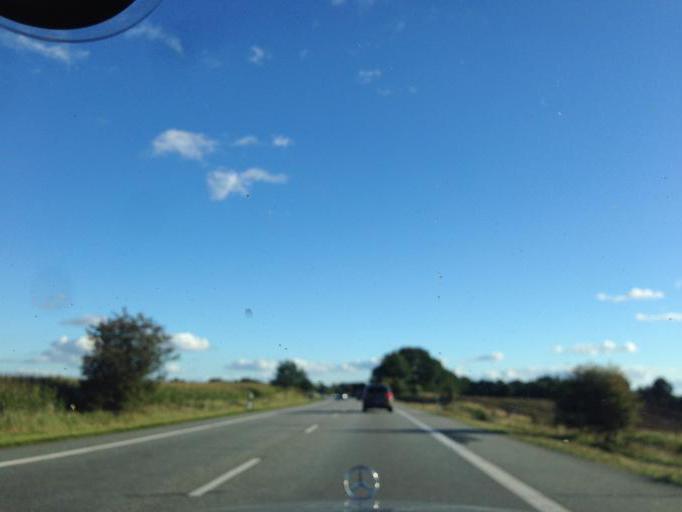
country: DE
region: Schleswig-Holstein
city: Rickling
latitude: 53.9921
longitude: 10.1844
